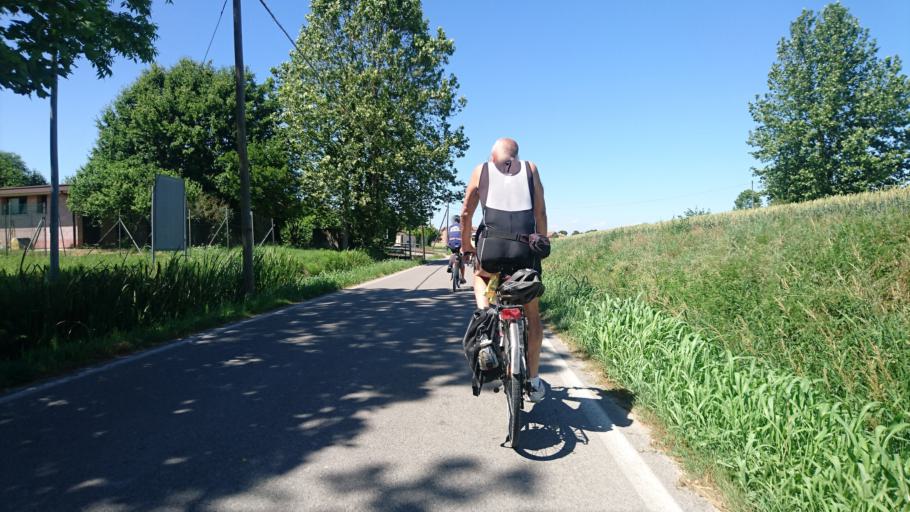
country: IT
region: Veneto
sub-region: Provincia di Padova
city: Bertipaglia
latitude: 45.3089
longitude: 11.8865
